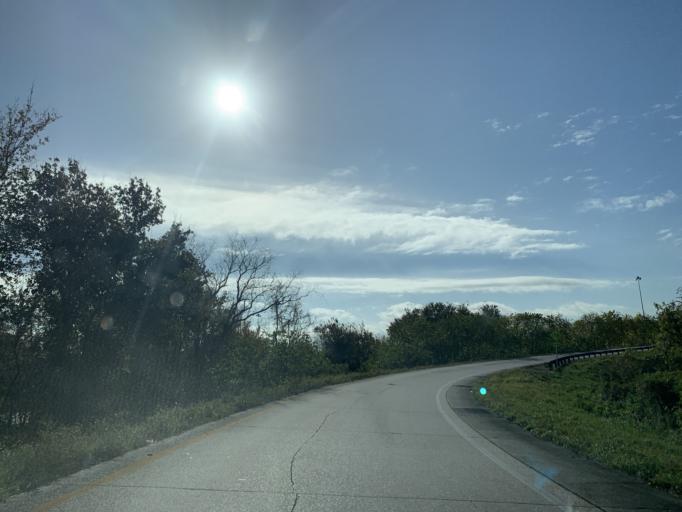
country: US
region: Florida
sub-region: Hillsborough County
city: Mango
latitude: 27.9829
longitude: -82.3242
